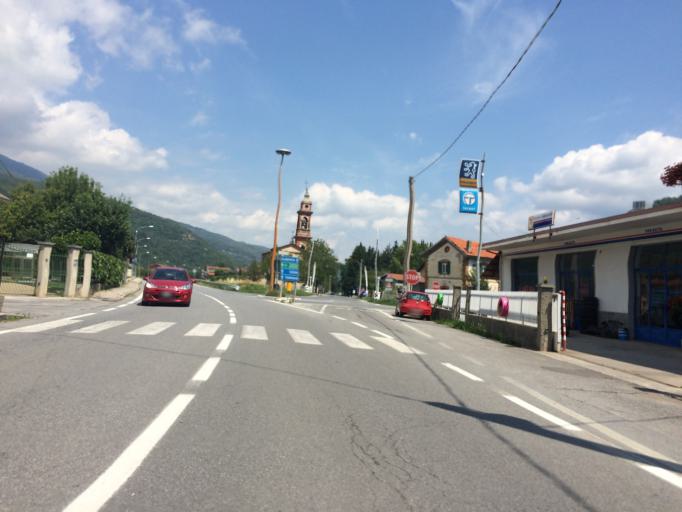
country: IT
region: Piedmont
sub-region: Provincia di Cuneo
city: Garessio
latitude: 44.2093
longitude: 8.0149
